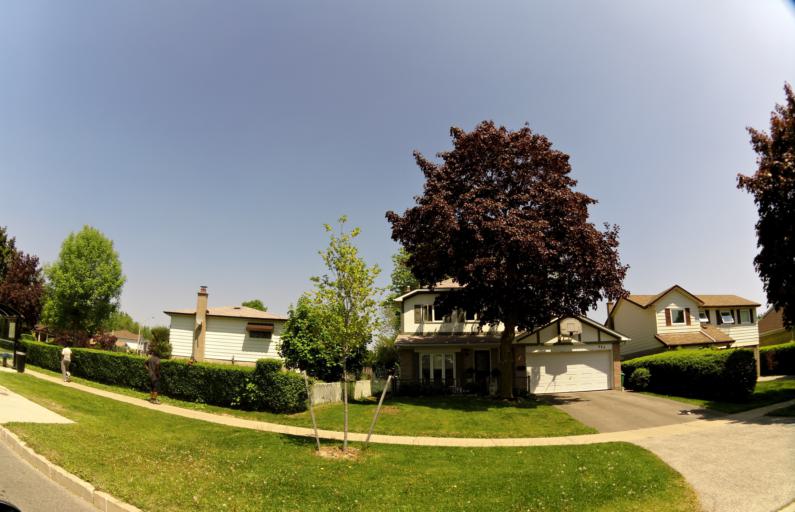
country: CA
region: Ontario
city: Mississauga
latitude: 43.5959
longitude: -79.6108
